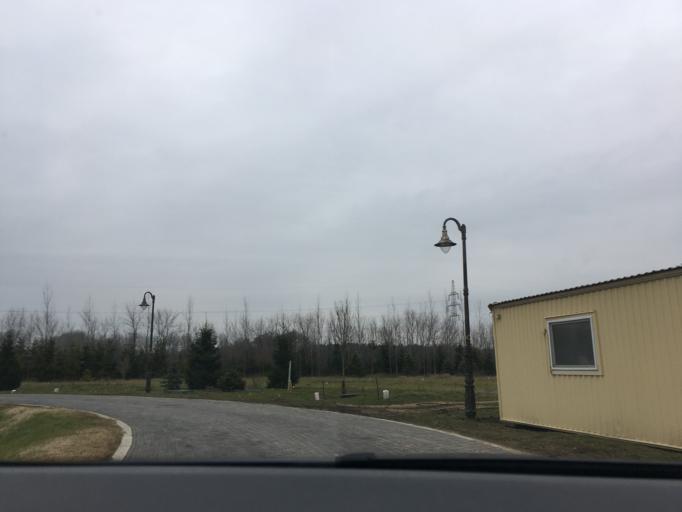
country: HU
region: Hajdu-Bihar
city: Debrecen
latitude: 47.5525
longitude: 21.6900
